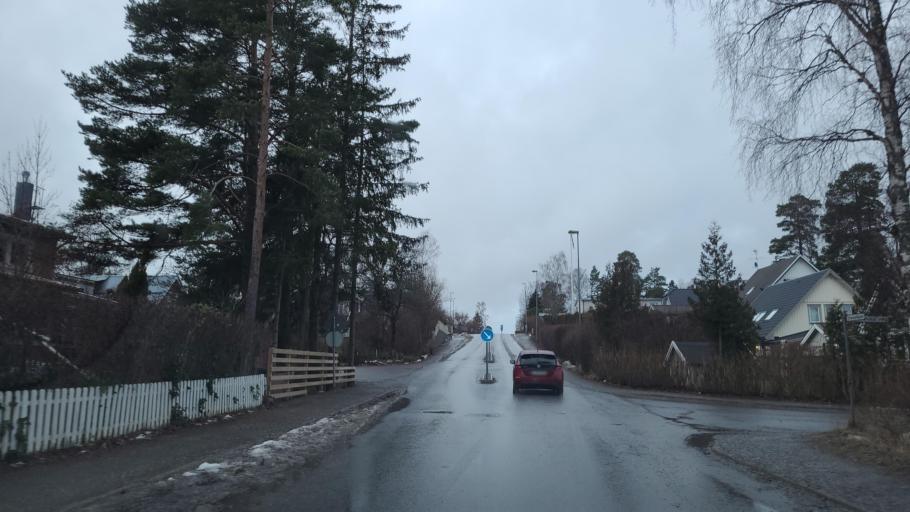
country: SE
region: Stockholm
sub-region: Taby Kommun
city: Taby
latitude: 59.4587
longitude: 18.0890
